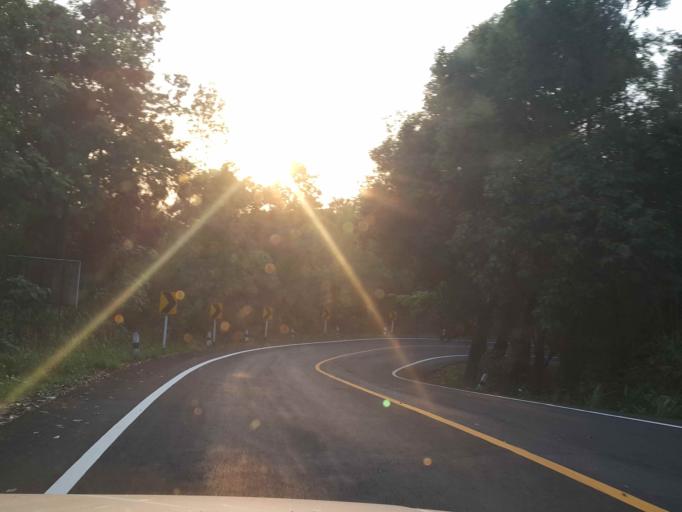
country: TH
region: Chiang Mai
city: Mae On
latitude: 19.0075
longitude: 99.3226
